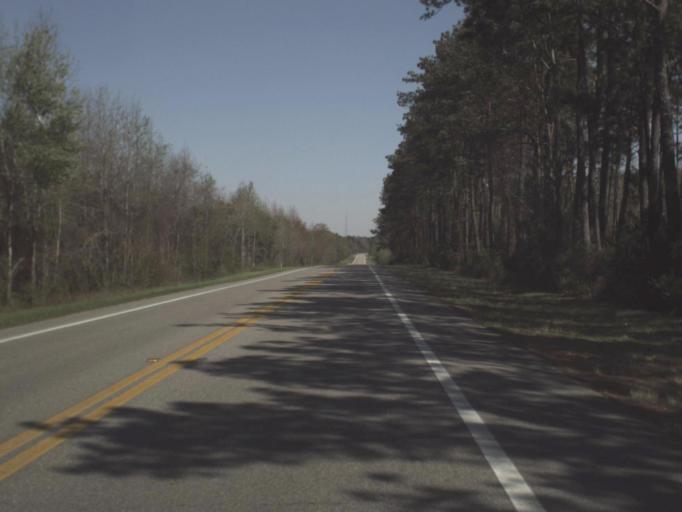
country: US
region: Florida
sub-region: Gadsden County
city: Quincy
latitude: 30.3879
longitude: -84.6767
